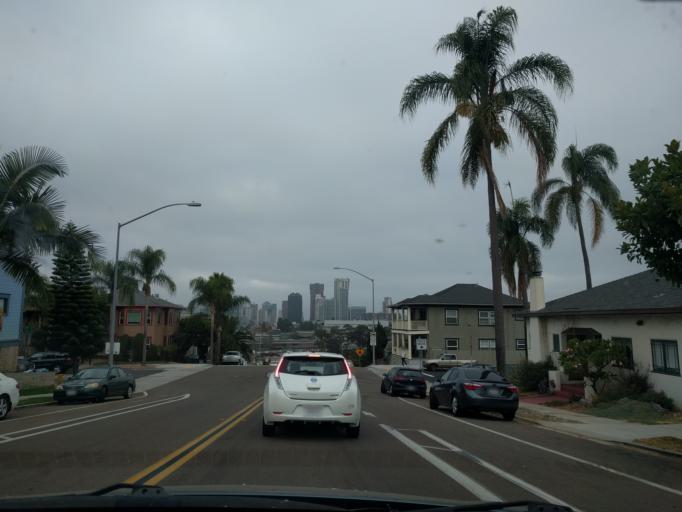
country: US
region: California
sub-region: San Diego County
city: San Diego
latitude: 32.7179
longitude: -117.1436
